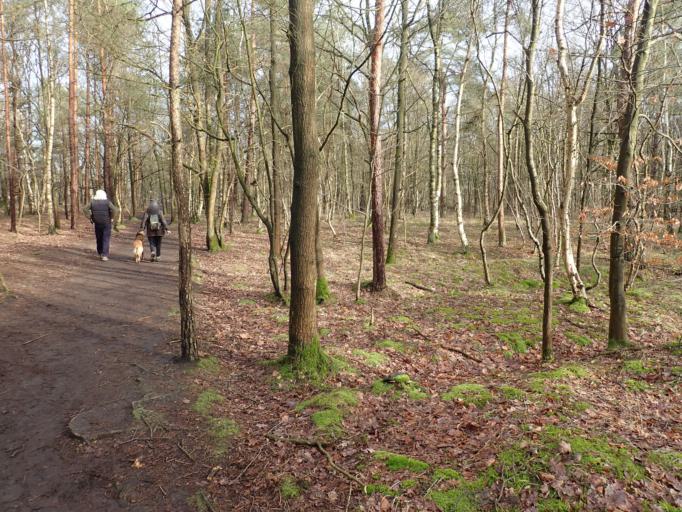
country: BE
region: Flanders
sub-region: Provincie Antwerpen
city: Nijlen
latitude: 51.1617
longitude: 4.6330
